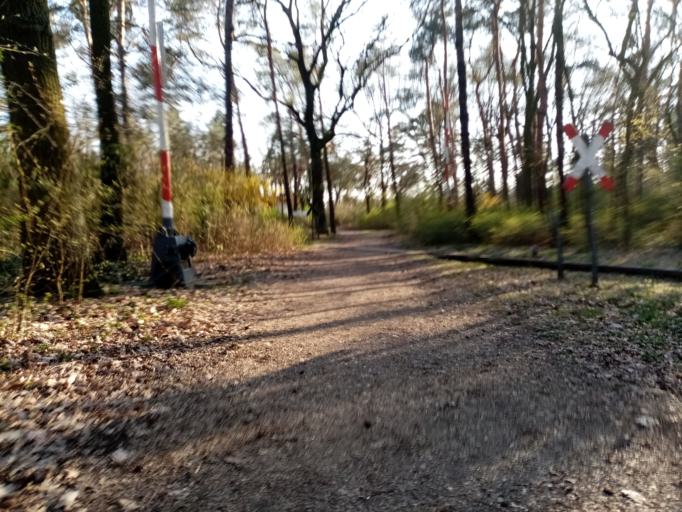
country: DE
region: Berlin
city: Oberschoneweide
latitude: 52.4618
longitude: 13.5436
